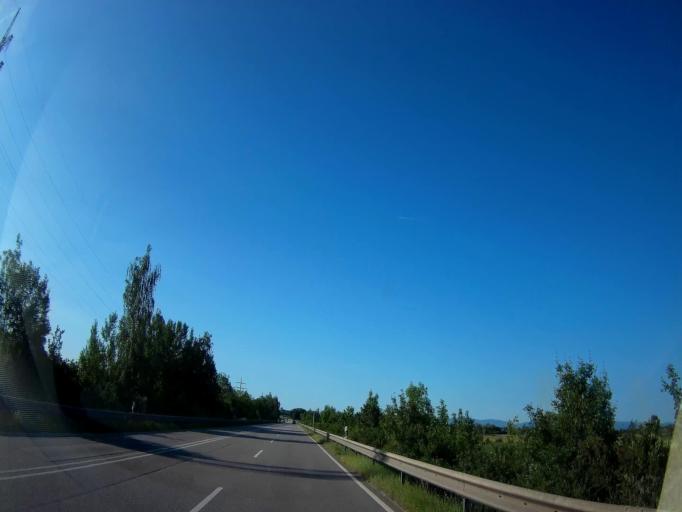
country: DE
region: Bavaria
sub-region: Lower Bavaria
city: Pilsting
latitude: 48.6990
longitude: 12.6750
